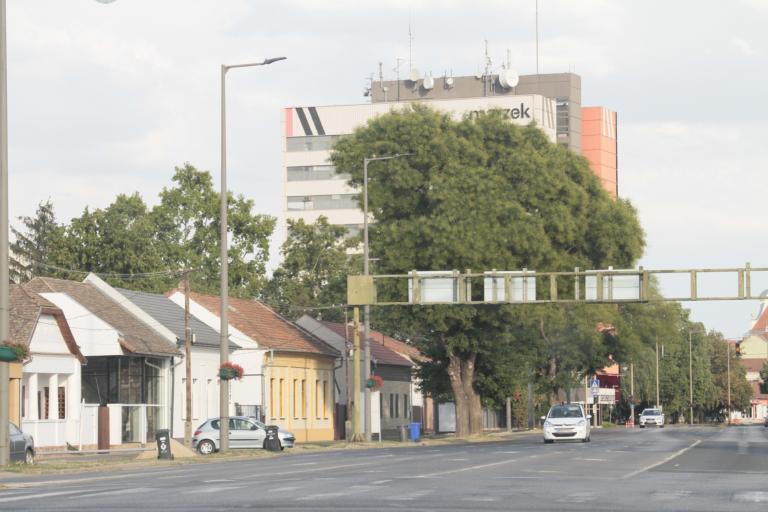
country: HU
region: Bekes
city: Bekescsaba
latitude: 46.6862
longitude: 21.0889
